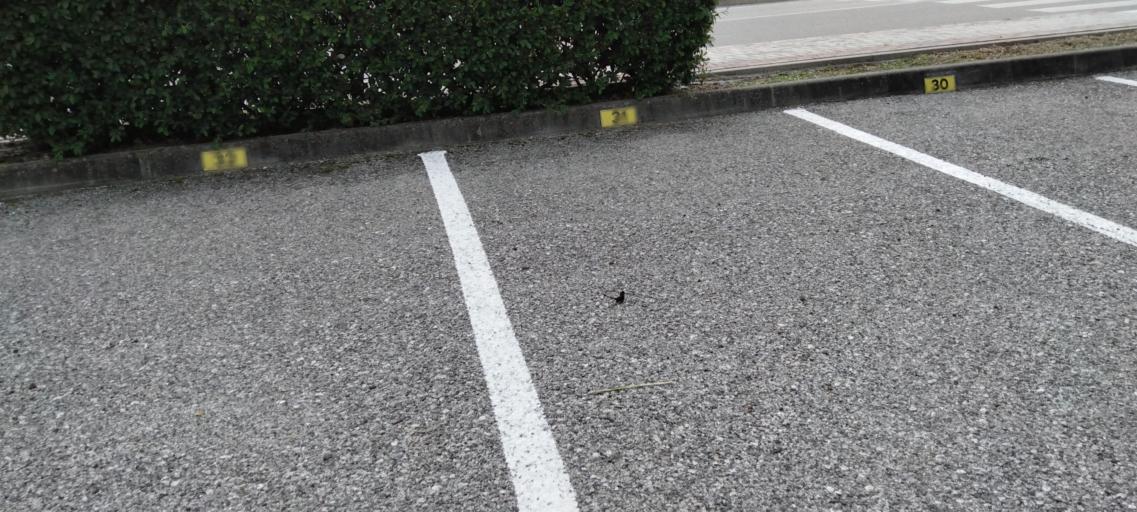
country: IT
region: Veneto
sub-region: Provincia di Padova
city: Camposampiero
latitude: 45.5608
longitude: 11.9276
